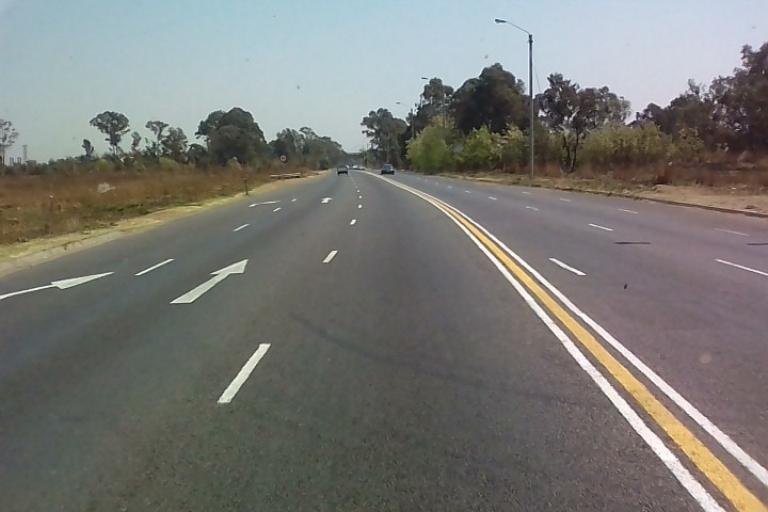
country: ZA
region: Gauteng
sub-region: Ekurhuleni Metropolitan Municipality
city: Boksburg
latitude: -26.2188
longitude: 28.2315
